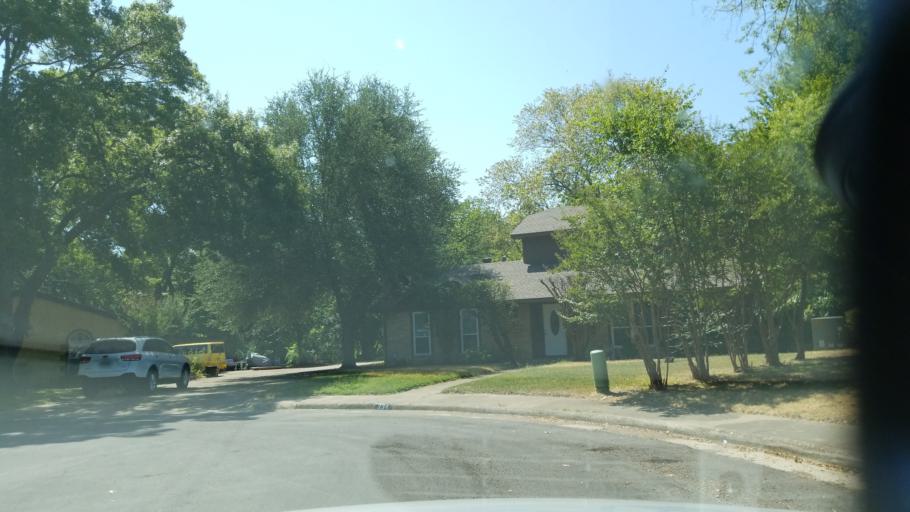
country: US
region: Texas
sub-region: Dallas County
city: Duncanville
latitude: 32.6501
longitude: -96.8938
